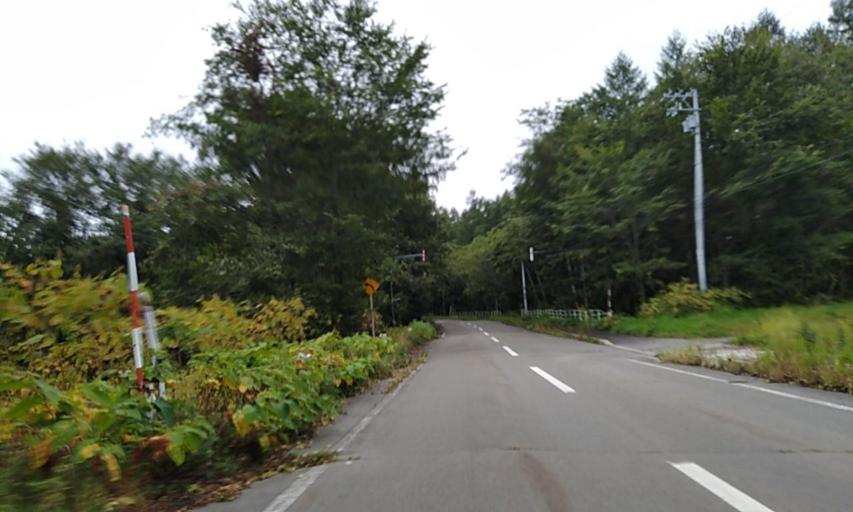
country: JP
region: Hokkaido
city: Obihiro
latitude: 42.6720
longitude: 143.0442
